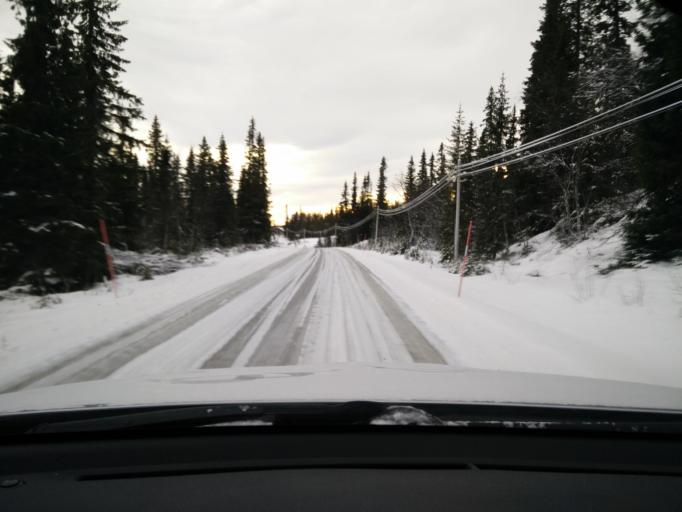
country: SE
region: Jaemtland
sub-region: Bergs Kommun
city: Hoverberg
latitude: 62.4830
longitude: 14.1216
